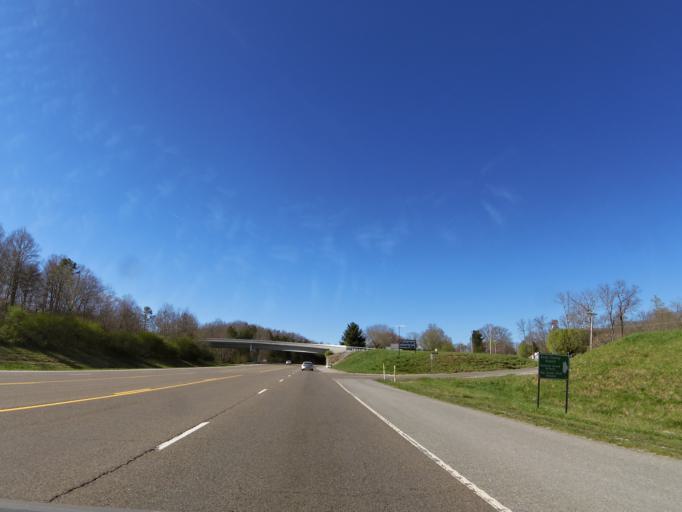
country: US
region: Tennessee
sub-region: Scott County
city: Oneida
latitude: 36.4571
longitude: -84.5467
